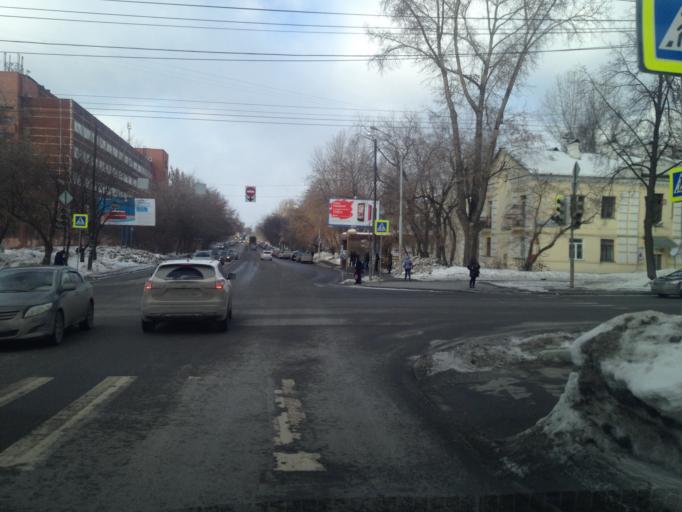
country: RU
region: Sverdlovsk
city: Yekaterinburg
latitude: 56.8468
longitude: 60.6575
